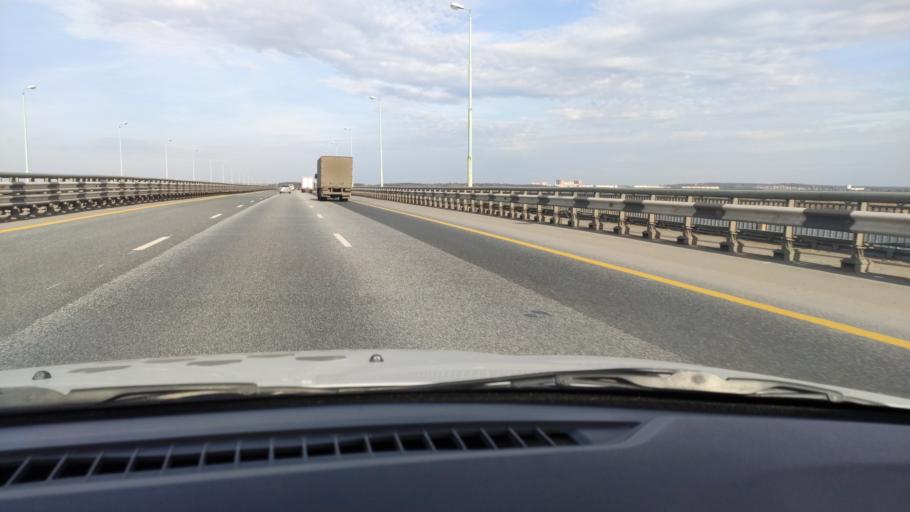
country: RU
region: Perm
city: Kondratovo
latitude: 58.0168
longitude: 56.0541
